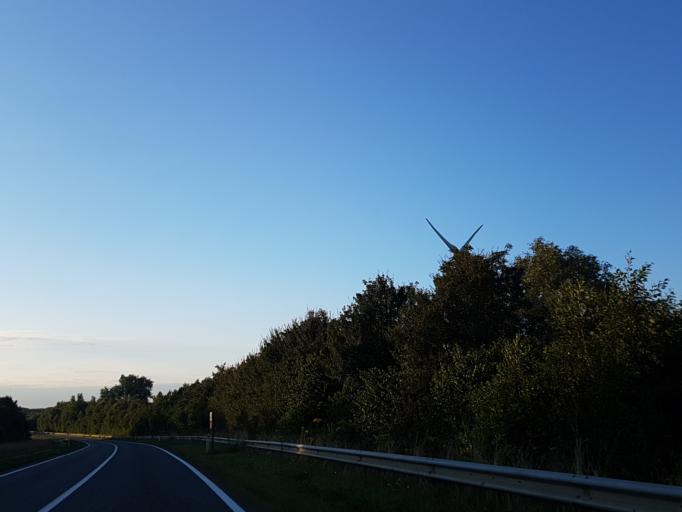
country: BE
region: Flanders
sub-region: Provincie Oost-Vlaanderen
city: Lebbeke
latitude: 51.0227
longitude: 4.1355
